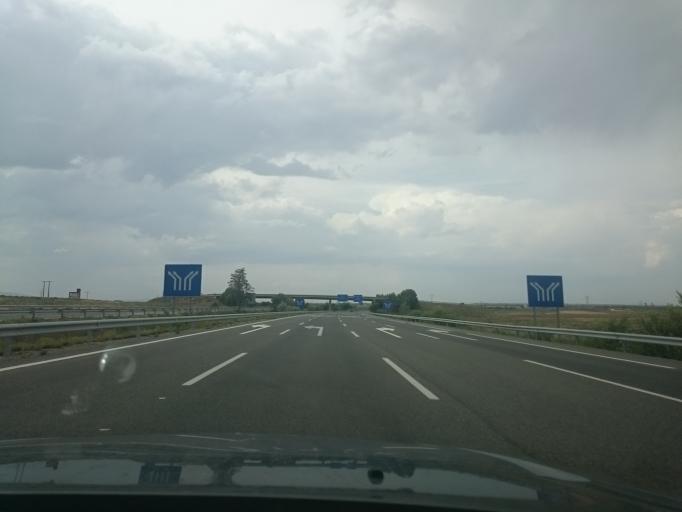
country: ES
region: Navarre
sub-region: Provincia de Navarra
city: Corella
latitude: 42.0891
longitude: -1.7168
